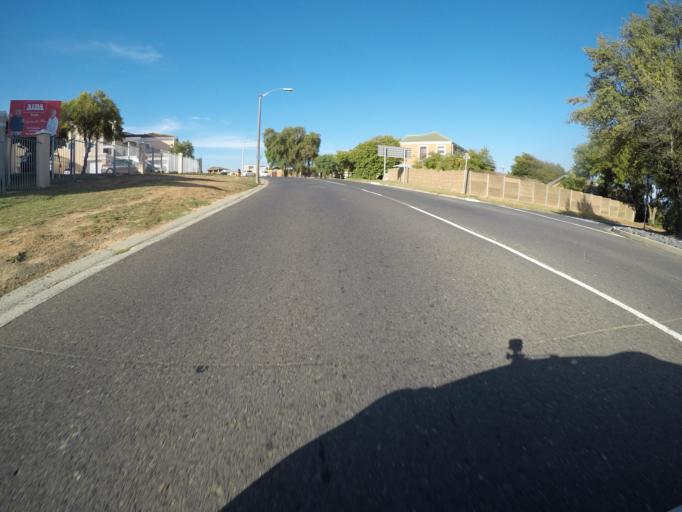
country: ZA
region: Western Cape
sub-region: City of Cape Town
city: Kraaifontein
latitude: -33.8786
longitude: 18.6450
